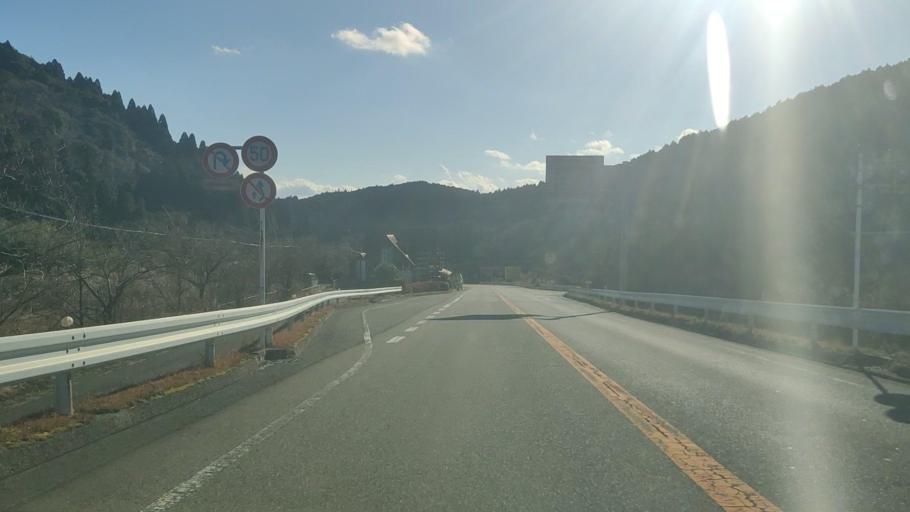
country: JP
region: Fukuoka
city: Maebaru-chuo
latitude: 33.4612
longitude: 130.2745
